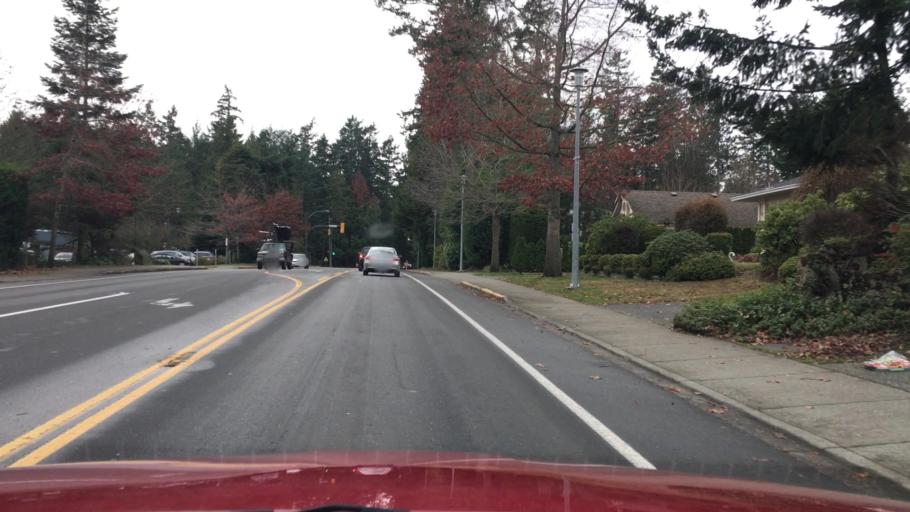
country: CA
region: British Columbia
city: Victoria
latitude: 48.5022
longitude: -123.3601
